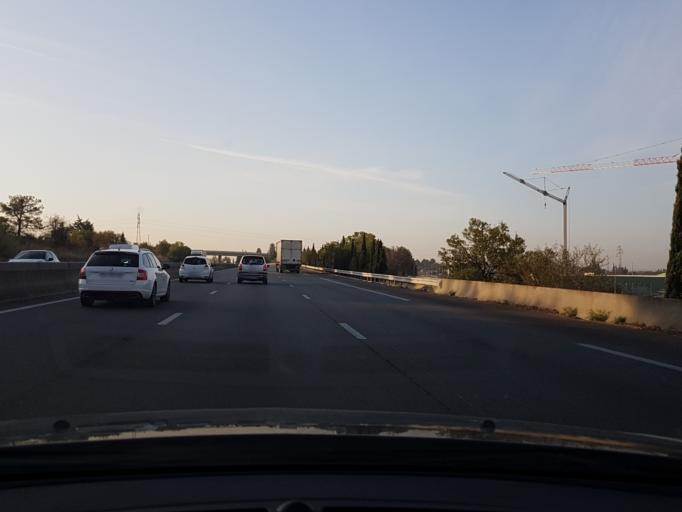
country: FR
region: Provence-Alpes-Cote d'Azur
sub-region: Departement du Vaucluse
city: Vedene
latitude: 43.9701
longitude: 4.8969
